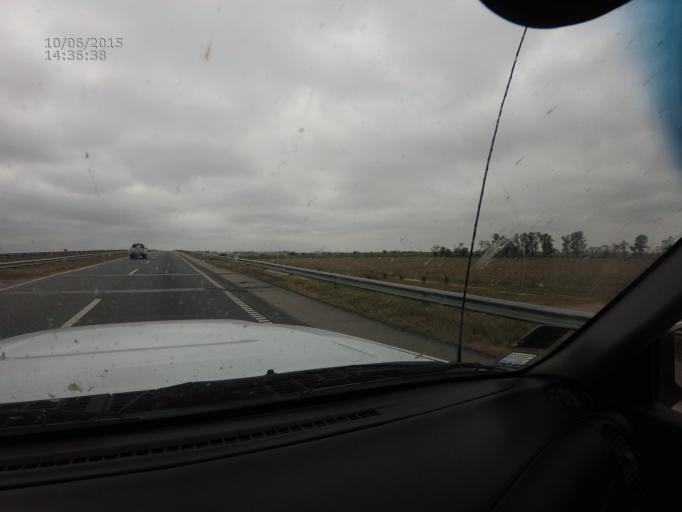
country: AR
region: Cordoba
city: James Craik
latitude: -32.1198
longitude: -63.4498
